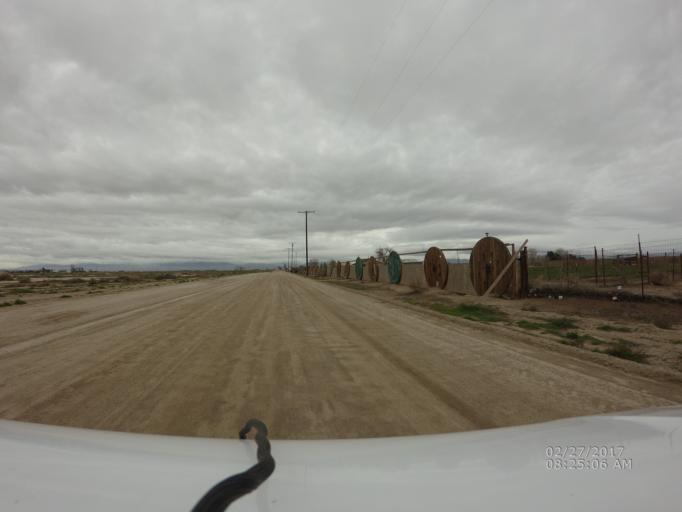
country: US
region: California
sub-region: Los Angeles County
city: Lancaster
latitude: 34.7170
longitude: -118.0144
